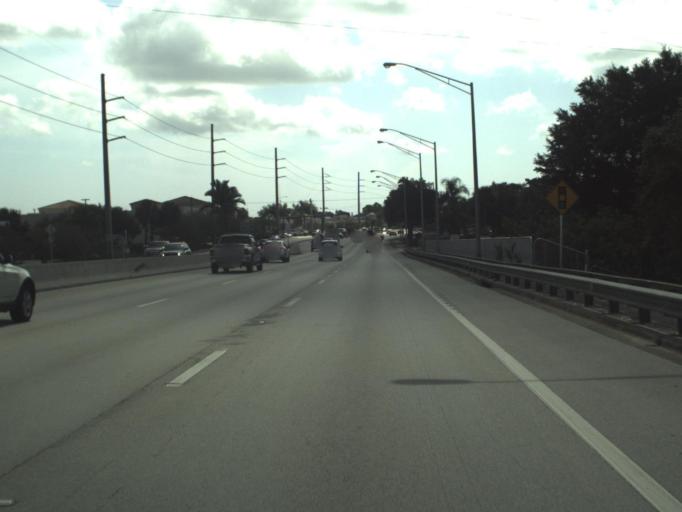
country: US
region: Florida
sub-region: Saint Lucie County
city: Port Saint Lucie
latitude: 27.2717
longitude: -80.3208
